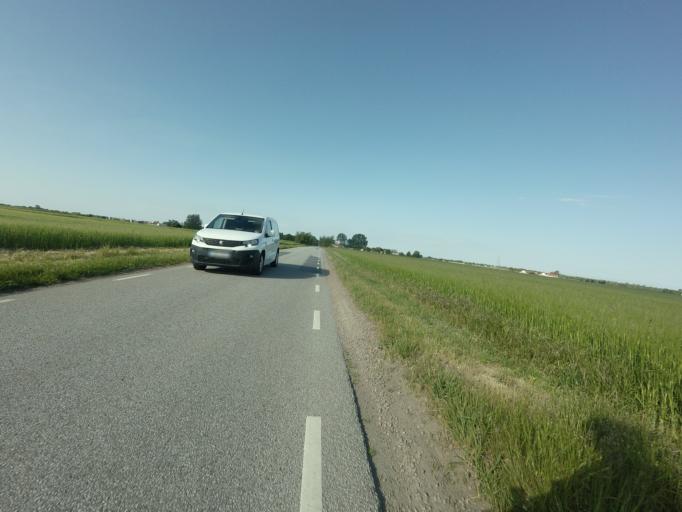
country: SE
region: Skane
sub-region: Trelleborgs Kommun
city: Skare
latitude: 55.4179
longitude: 13.0162
